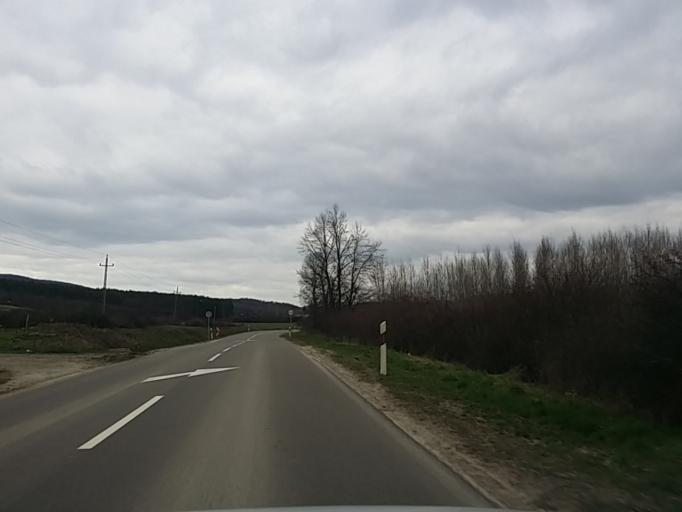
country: HU
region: Heves
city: Verpelet
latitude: 47.8688
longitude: 20.1997
